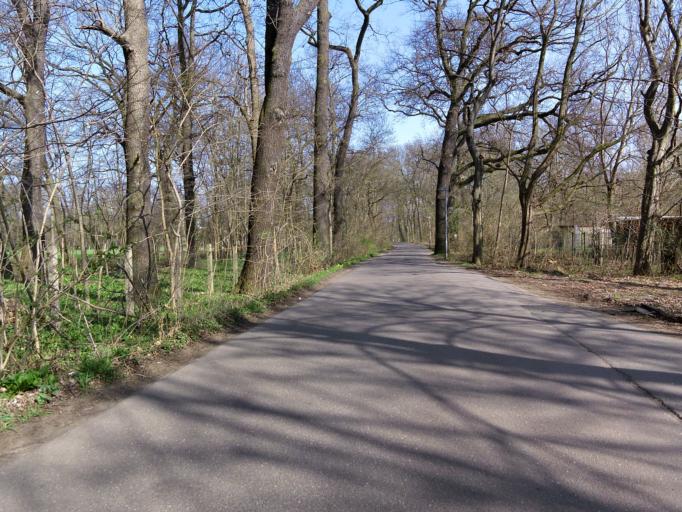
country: DE
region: Saxony
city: Leipzig
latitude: 51.3720
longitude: 12.3103
